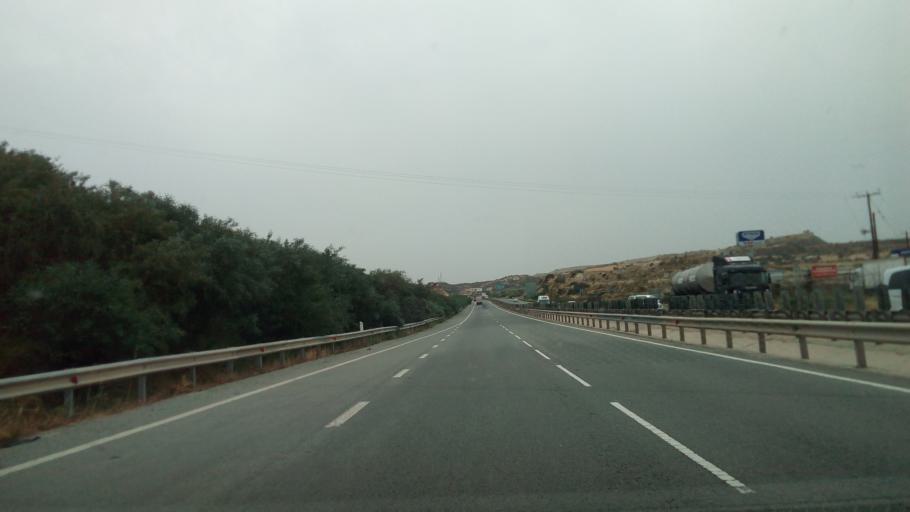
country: CY
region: Larnaka
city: Kofinou
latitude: 34.7958
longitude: 33.3469
